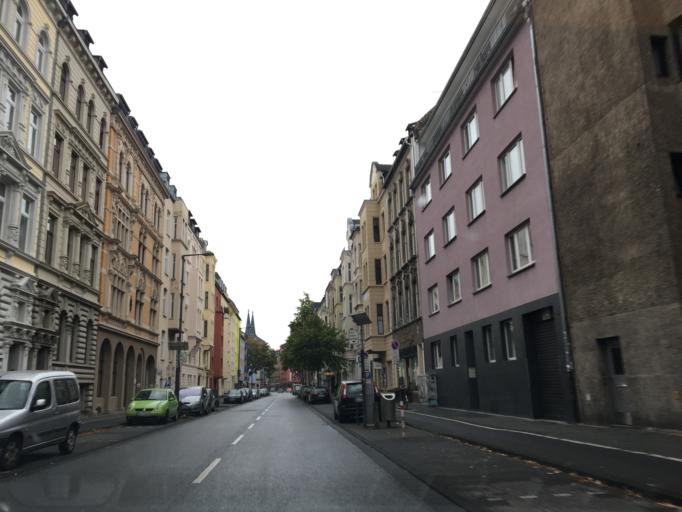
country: DE
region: North Rhine-Westphalia
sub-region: Regierungsbezirk Koln
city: Neustadt/Nord
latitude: 50.9518
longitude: 6.9520
